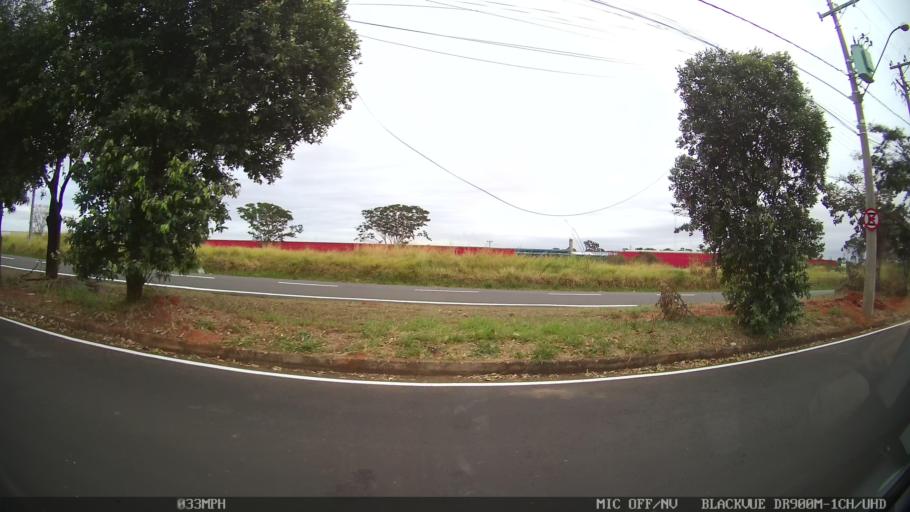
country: BR
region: Sao Paulo
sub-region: Sao Jose Do Rio Preto
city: Sao Jose do Rio Preto
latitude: -20.8259
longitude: -49.4221
